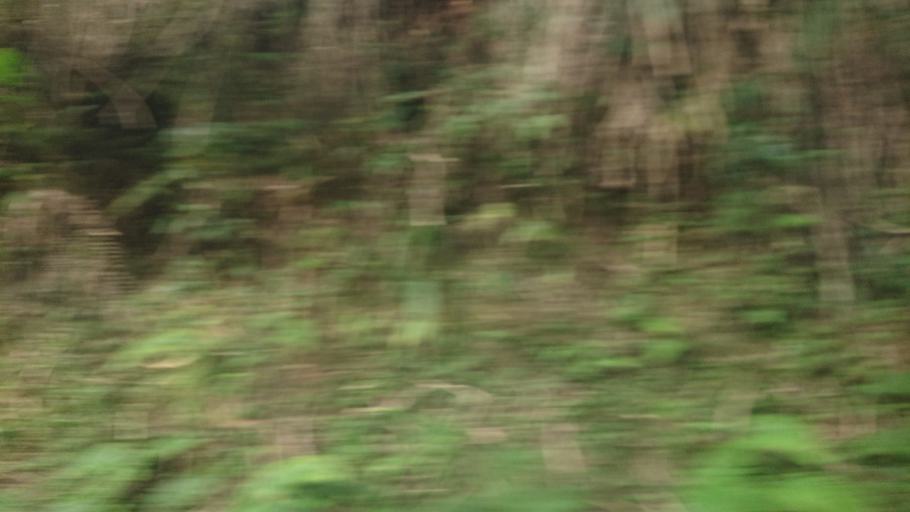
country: TW
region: Taiwan
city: Lugu
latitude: 23.4993
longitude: 120.7882
